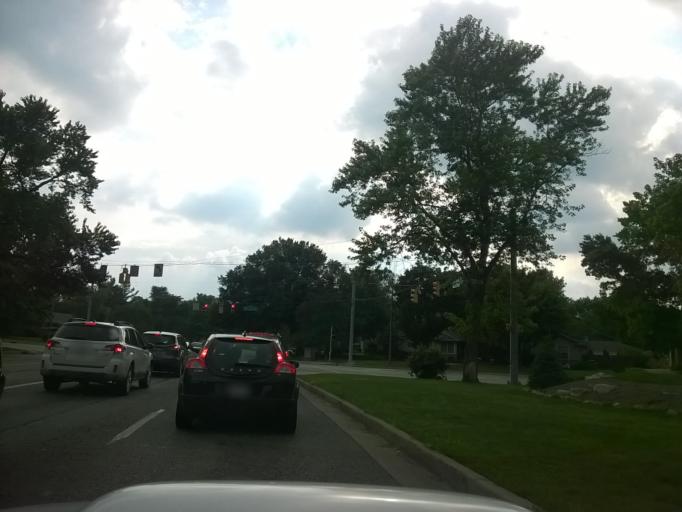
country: US
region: Indiana
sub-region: Marion County
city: Broad Ripple
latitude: 39.8631
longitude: -86.1568
